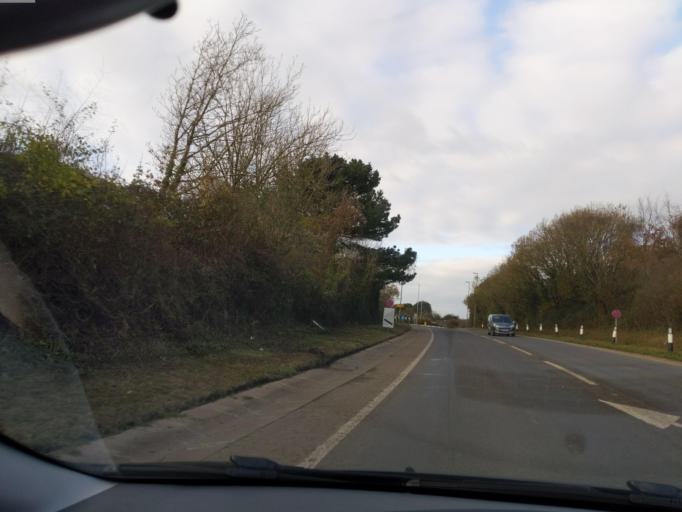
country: GB
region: England
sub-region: Cornwall
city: Wadebridge
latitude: 50.5216
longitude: -4.8201
